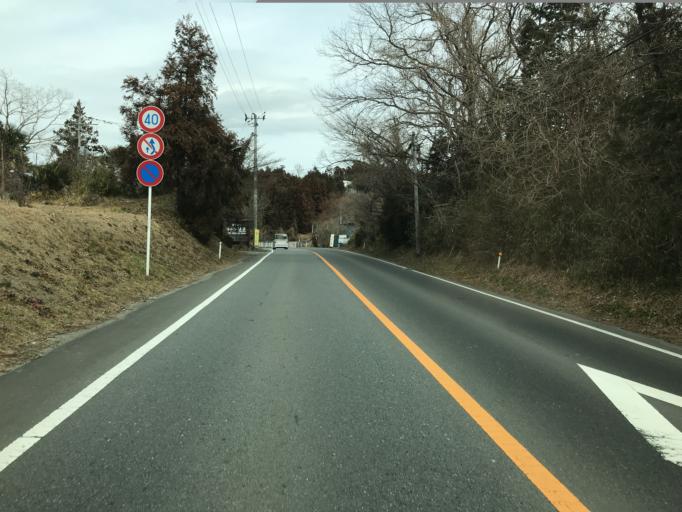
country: JP
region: Fukushima
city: Iwaki
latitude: 37.1025
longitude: 140.8761
